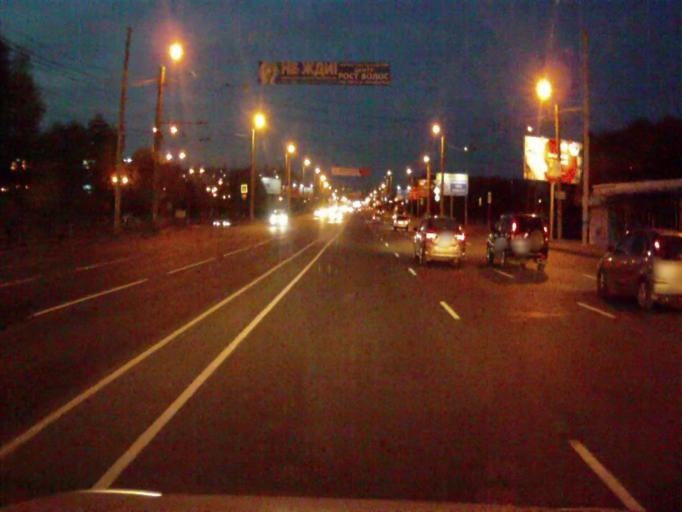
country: RU
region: Chelyabinsk
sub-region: Gorod Chelyabinsk
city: Chelyabinsk
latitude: 55.1715
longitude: 61.3582
